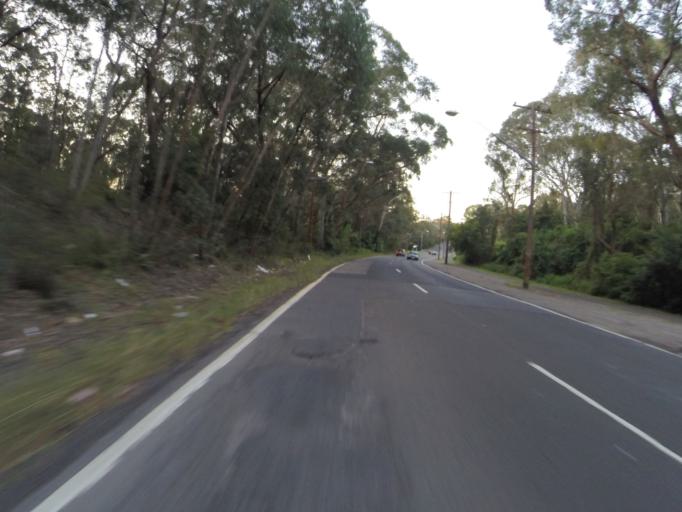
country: AU
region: New South Wales
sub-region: Bankstown
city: Revesby
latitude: -33.9702
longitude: 151.0150
